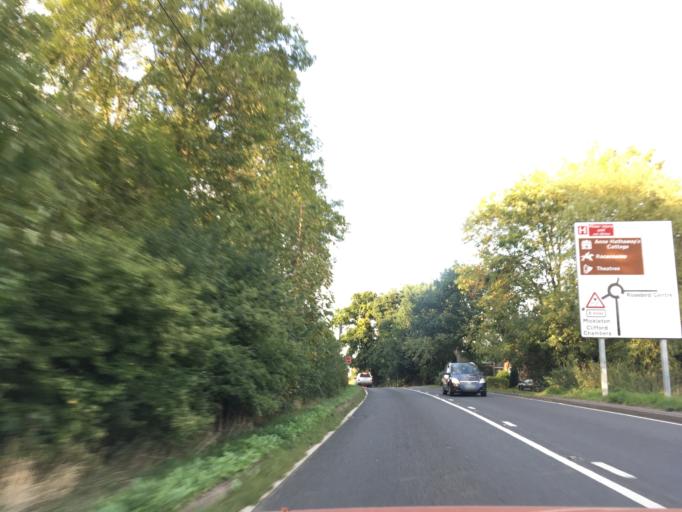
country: GB
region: England
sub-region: Warwickshire
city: Stratford-upon-Avon
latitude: 52.1776
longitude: -1.7013
